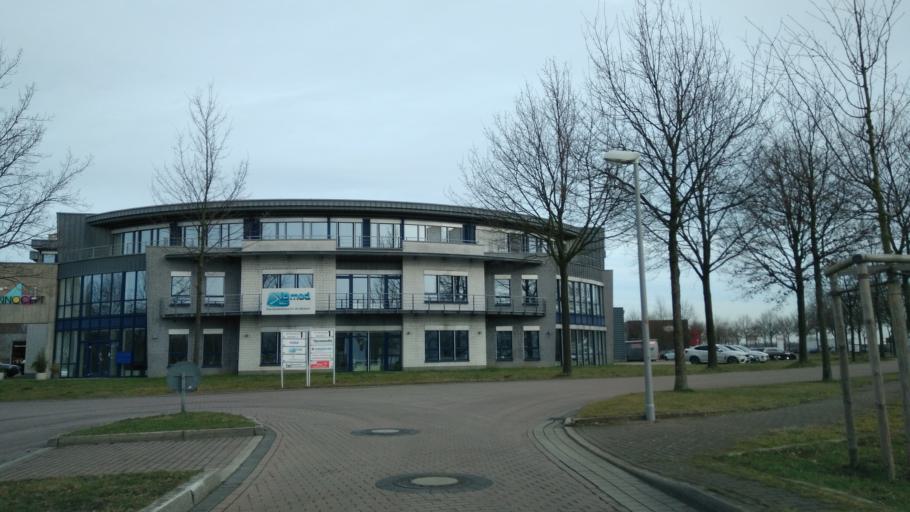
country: DE
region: North Rhine-Westphalia
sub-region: Regierungsbezirk Munster
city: Gladbeck
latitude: 51.5725
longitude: 6.9384
